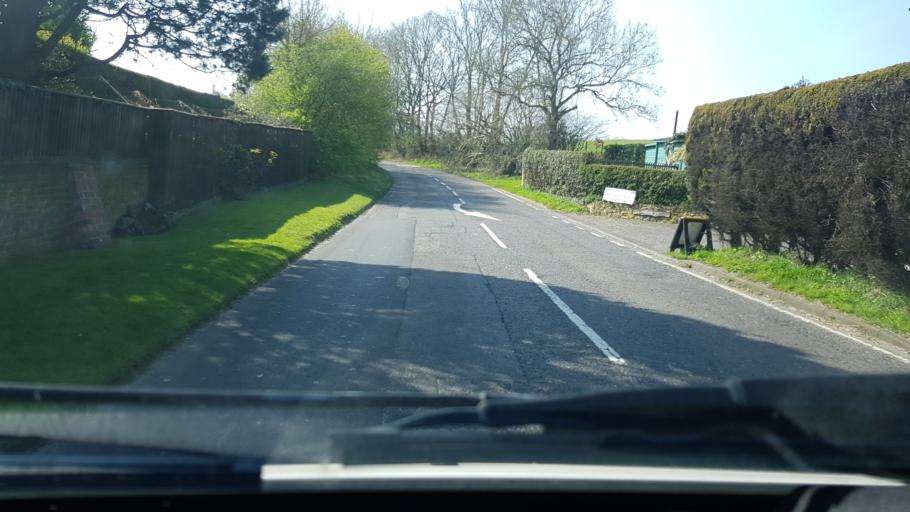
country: GB
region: England
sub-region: West Sussex
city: Fernhurst
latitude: 51.0375
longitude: -0.7240
